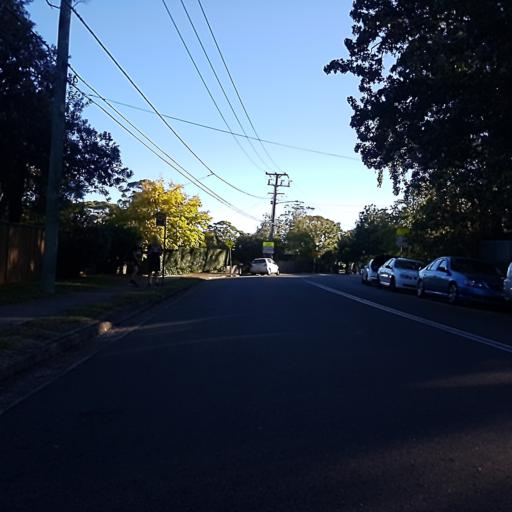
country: AU
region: New South Wales
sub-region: Warringah
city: Davidson
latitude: -33.7419
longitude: 151.2084
